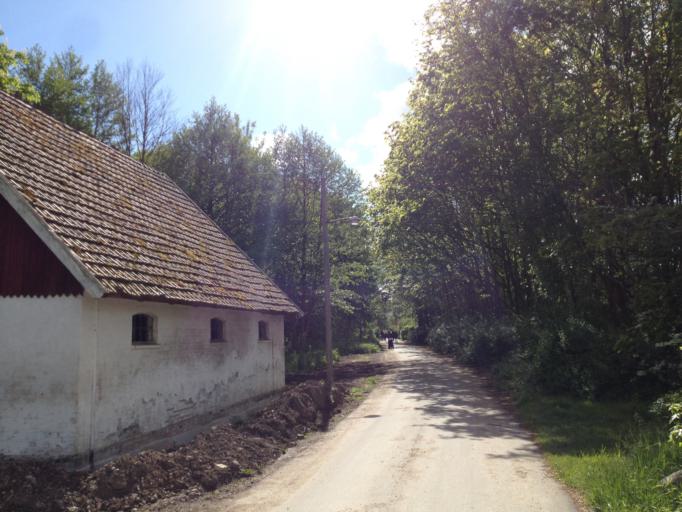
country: DK
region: Capital Region
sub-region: Fredensborg Kommune
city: Niva
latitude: 55.9303
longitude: 12.5145
